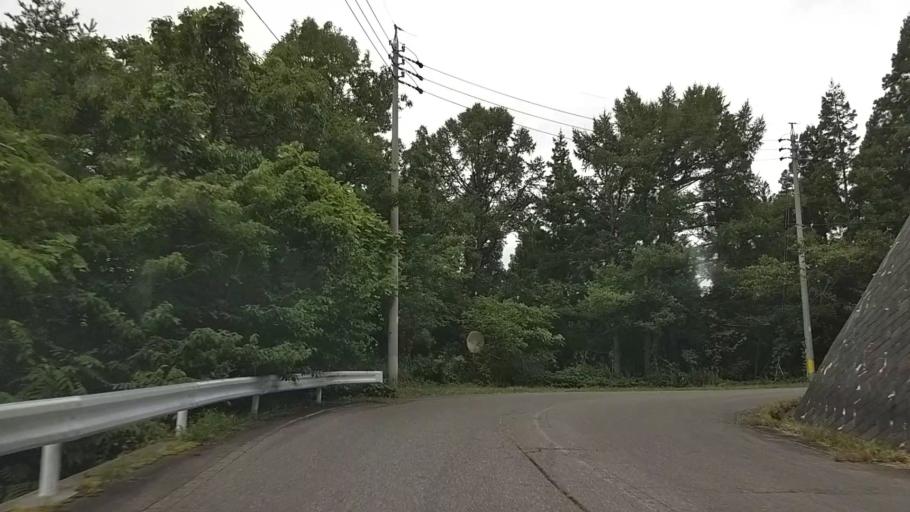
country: JP
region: Nagano
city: Iiyama
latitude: 36.8163
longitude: 138.3715
